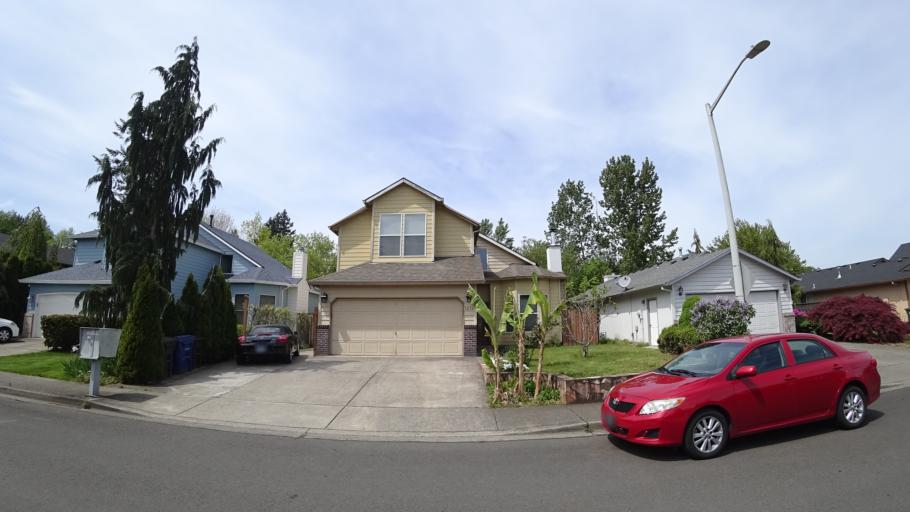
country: US
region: Oregon
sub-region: Clackamas County
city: Milwaukie
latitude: 45.4532
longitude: -122.6077
